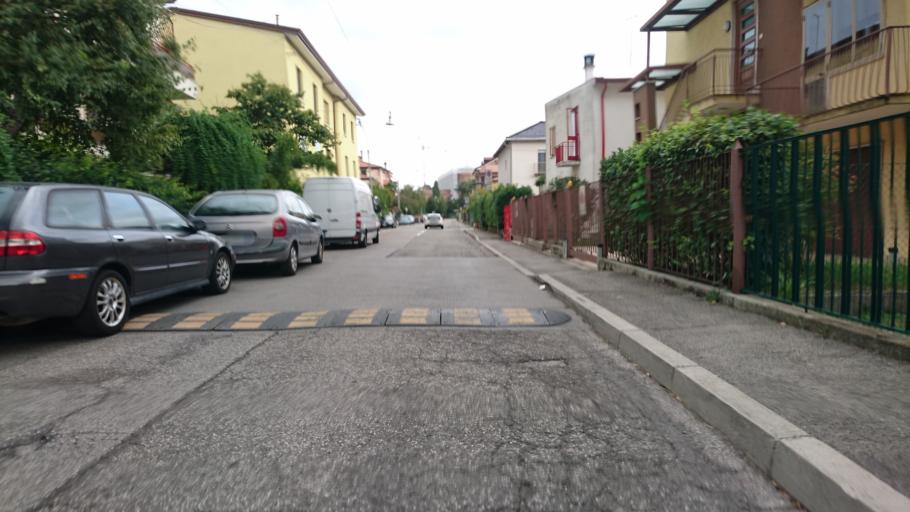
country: IT
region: Veneto
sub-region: Provincia di Padova
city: Padova
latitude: 45.4051
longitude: 11.8561
